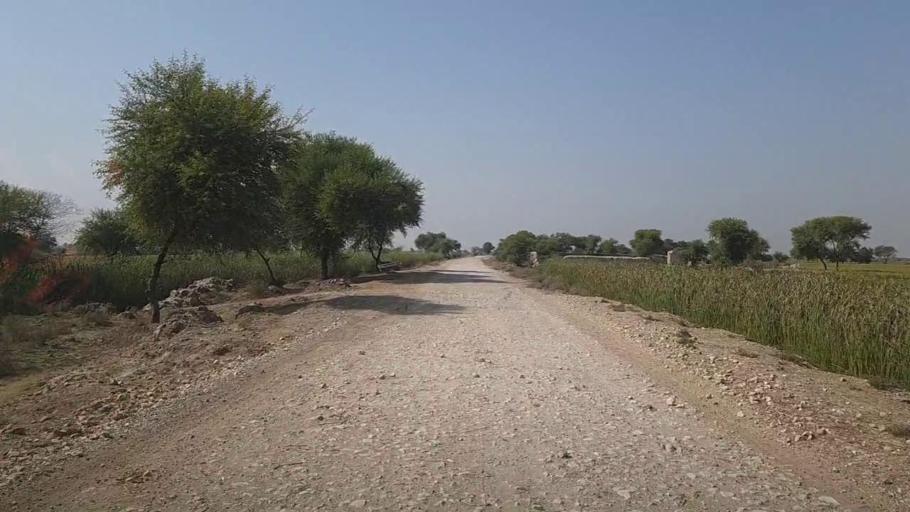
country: PK
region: Sindh
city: Kandhkot
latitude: 28.3937
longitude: 69.2781
